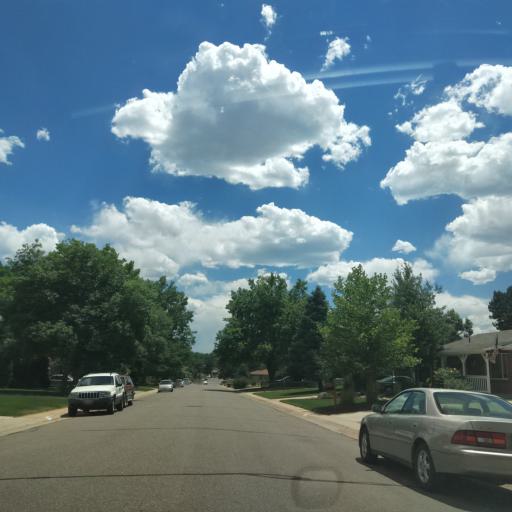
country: US
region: Colorado
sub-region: Jefferson County
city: Lakewood
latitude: 39.6848
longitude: -105.0918
